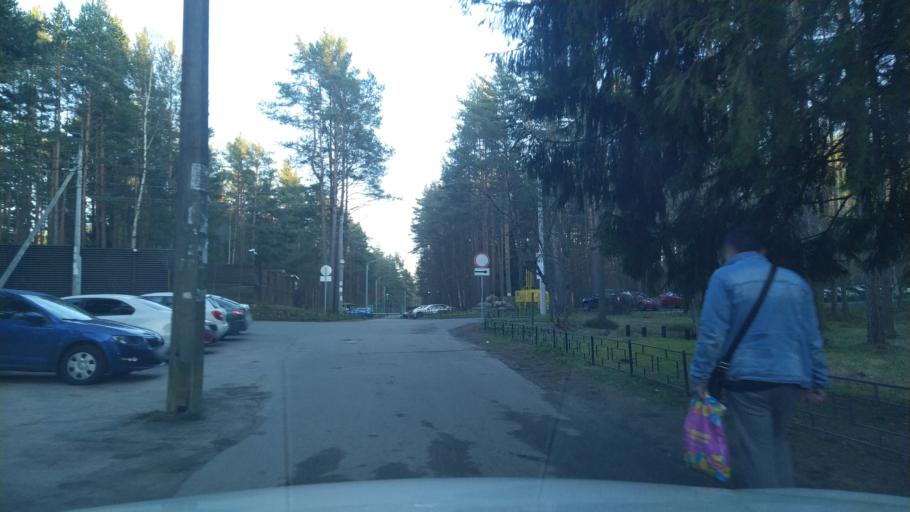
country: RU
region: St.-Petersburg
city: Solnechnoye
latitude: 60.1454
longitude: 29.9382
